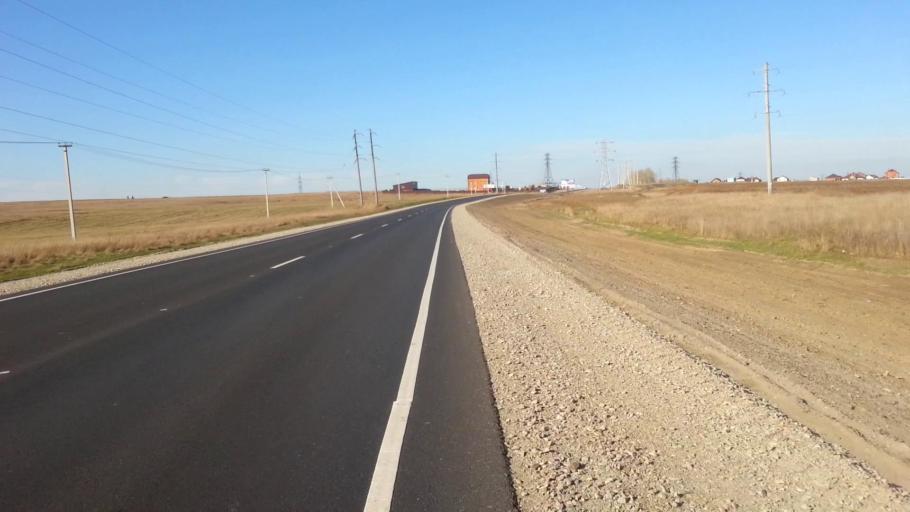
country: RU
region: Altai Krai
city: Sannikovo
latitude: 53.3315
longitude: 83.9386
